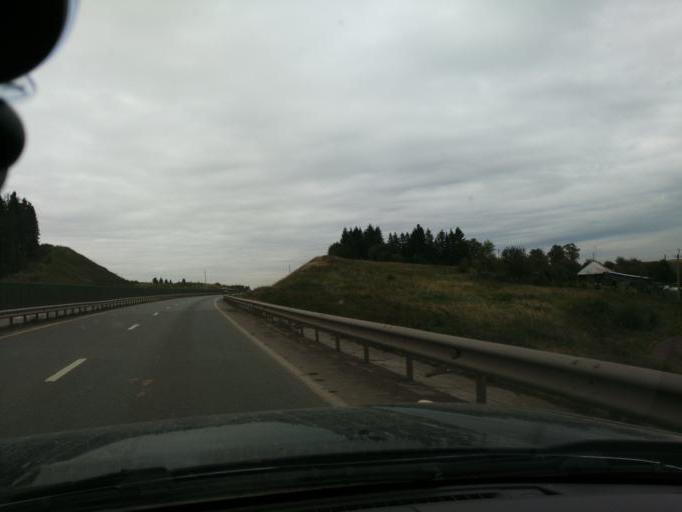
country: RU
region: Perm
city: Froly
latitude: 57.9349
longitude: 56.2158
